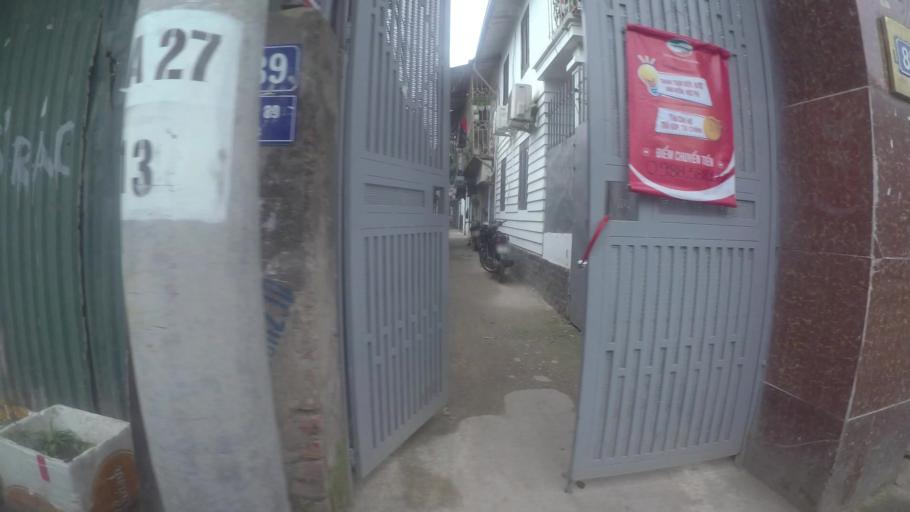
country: VN
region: Ha Noi
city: Tay Ho
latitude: 21.0709
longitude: 105.8278
